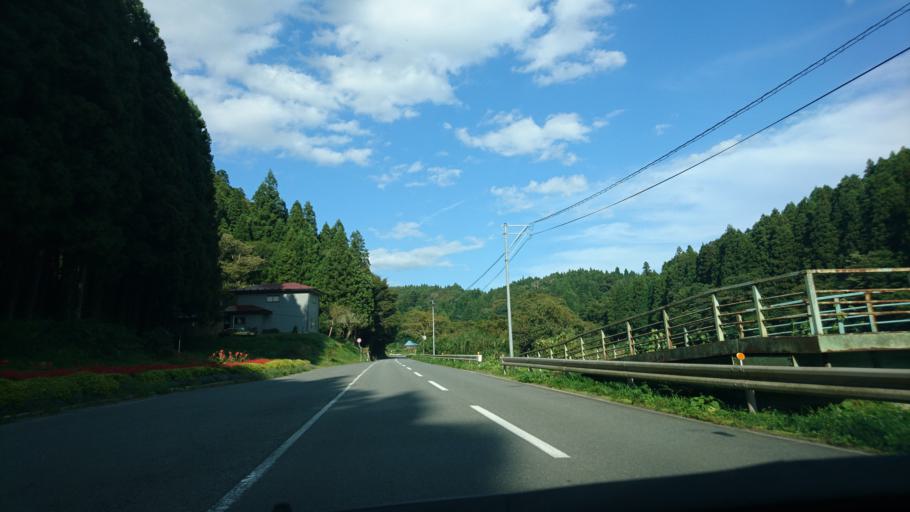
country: JP
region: Iwate
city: Ichinoseki
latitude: 38.8598
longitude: 141.3183
